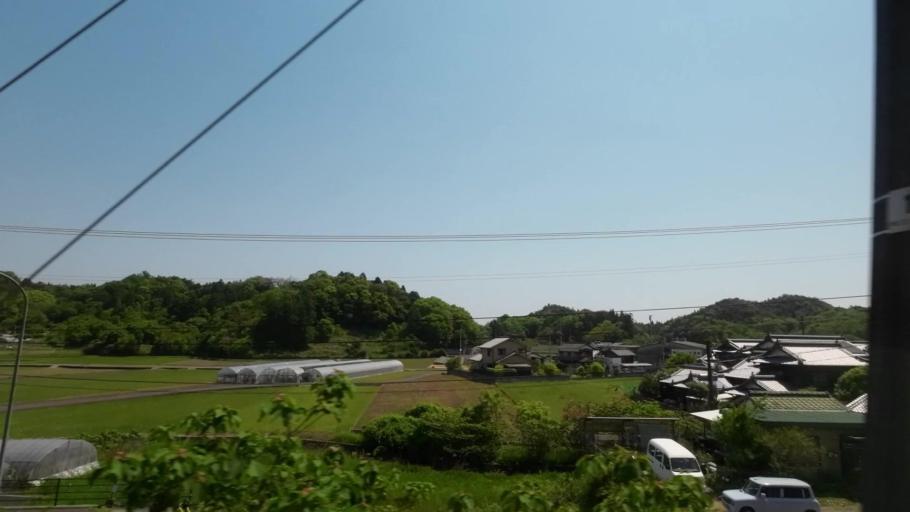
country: JP
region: Ehime
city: Saijo
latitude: 33.9900
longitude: 133.0520
